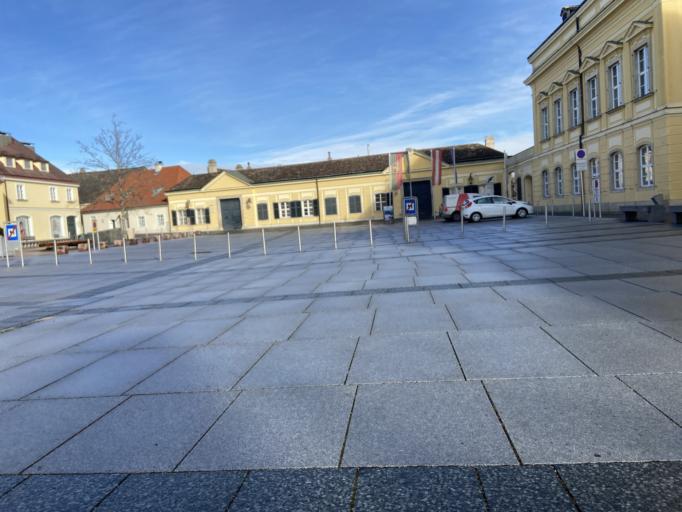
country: AT
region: Lower Austria
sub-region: Politischer Bezirk Modling
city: Laxenburg
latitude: 48.0684
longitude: 16.3580
